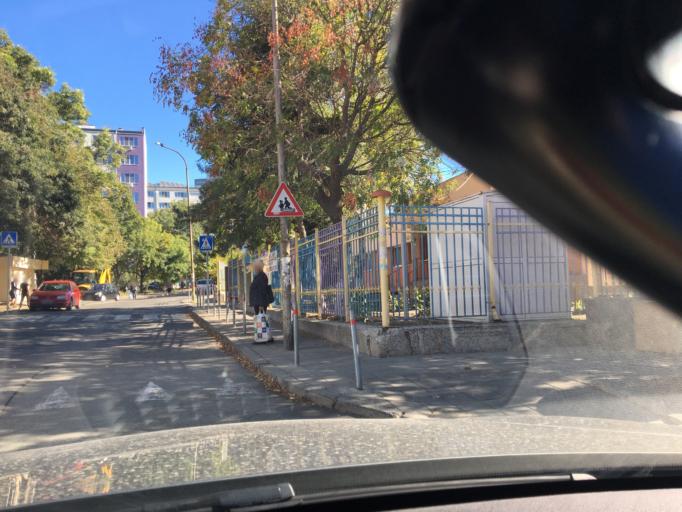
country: BG
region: Burgas
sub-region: Obshtina Burgas
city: Burgas
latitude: 42.5186
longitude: 27.4472
